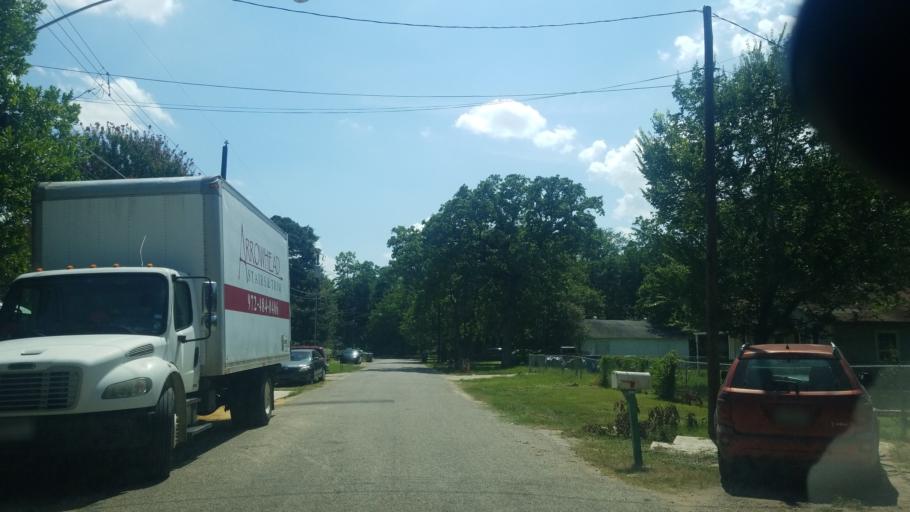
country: US
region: Texas
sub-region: Dallas County
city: Hutchins
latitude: 32.7147
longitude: -96.7437
